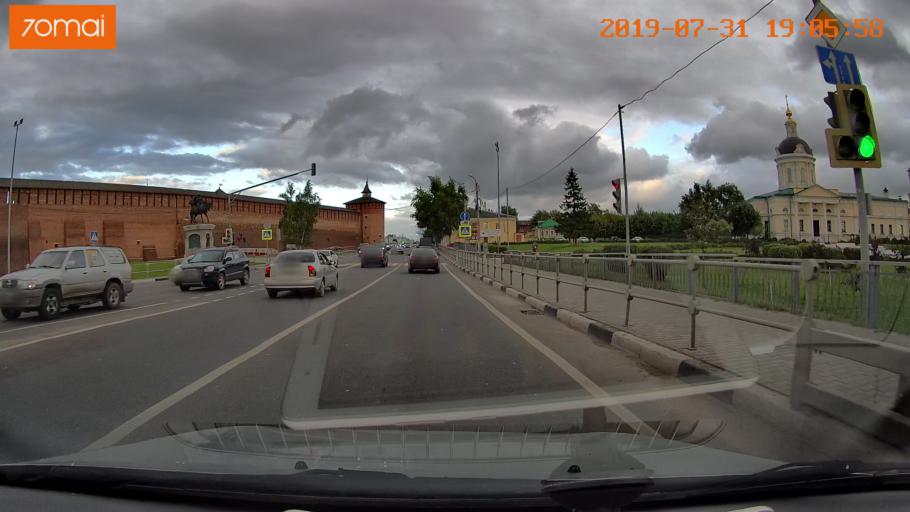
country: RU
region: Moskovskaya
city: Kolomna
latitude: 55.1042
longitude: 38.7496
